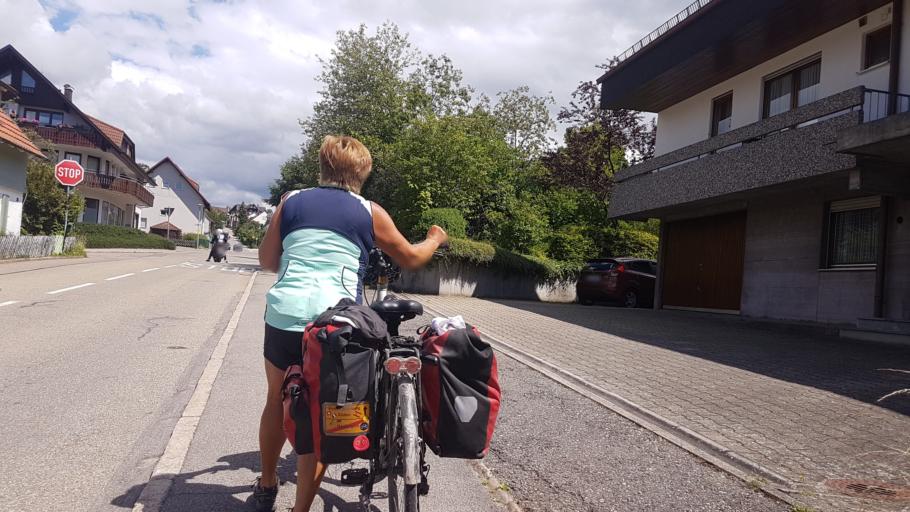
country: DE
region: Baden-Wuerttemberg
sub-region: Freiburg Region
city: Schramberg
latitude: 48.2275
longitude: 8.4142
